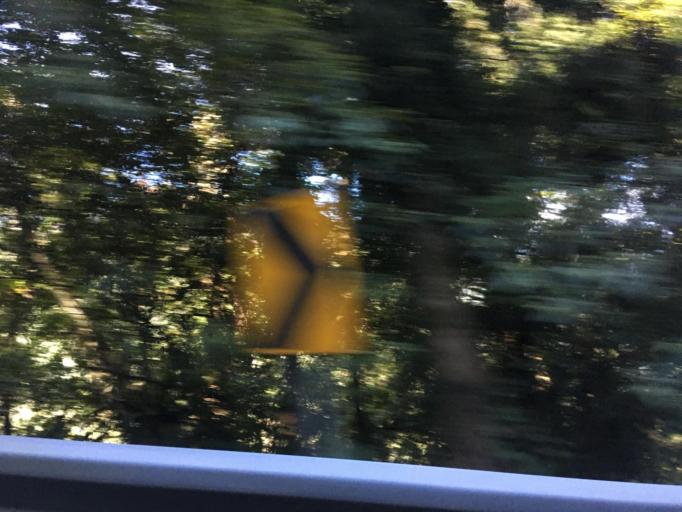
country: TW
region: Taiwan
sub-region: Yilan
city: Yilan
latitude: 24.5502
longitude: 121.5096
